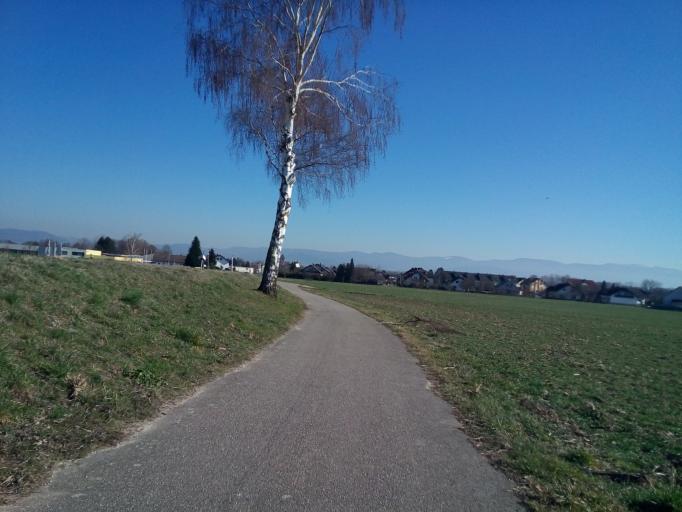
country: DE
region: Baden-Wuerttemberg
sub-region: Karlsruhe Region
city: Schwarzach
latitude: 48.7496
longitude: 8.0323
